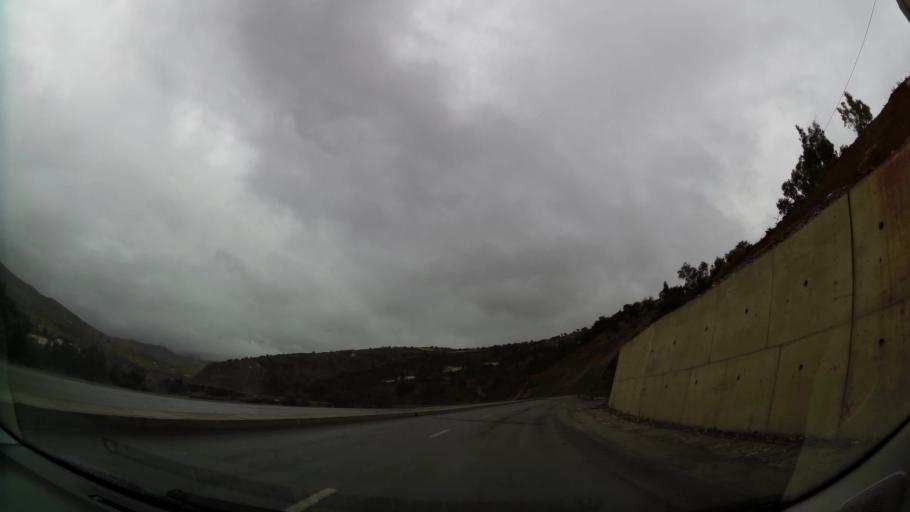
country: MA
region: Taza-Al Hoceima-Taounate
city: Imzourene
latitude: 35.0135
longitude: -3.8169
